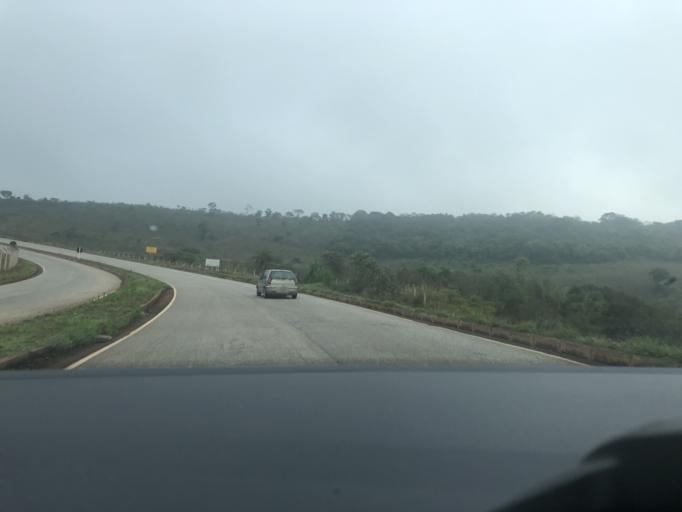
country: BR
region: Minas Gerais
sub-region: Congonhas
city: Congonhas
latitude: -20.5887
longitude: -43.9466
